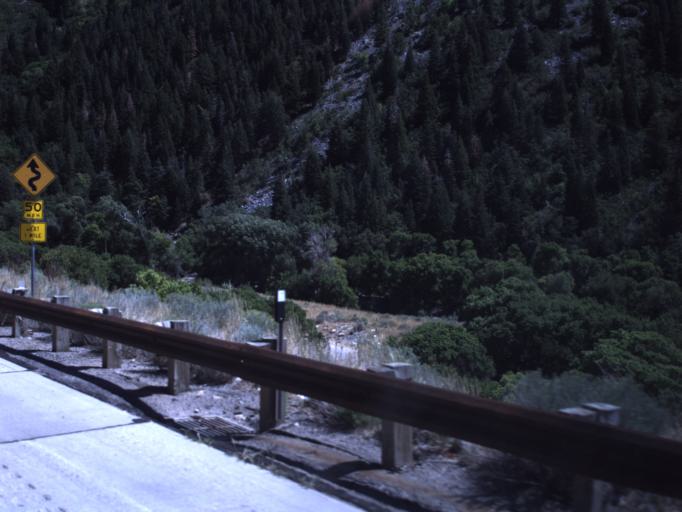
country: US
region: Utah
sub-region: Utah County
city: Orem
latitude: 40.3483
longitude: -111.5923
